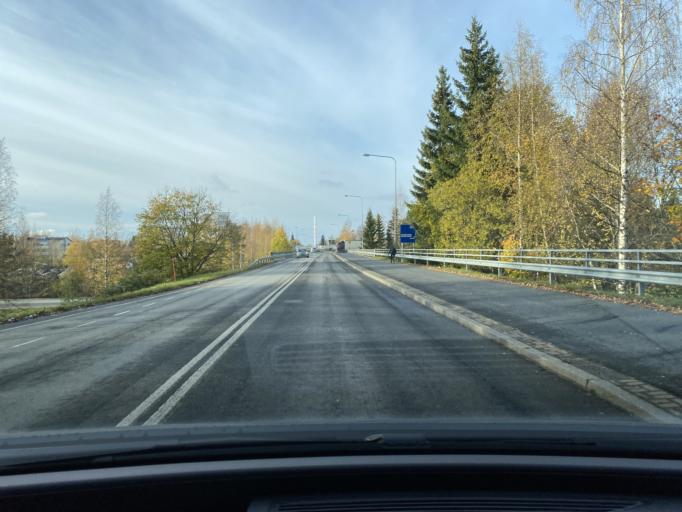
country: FI
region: Pirkanmaa
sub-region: Tampere
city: Lempaeaelae
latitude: 61.3111
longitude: 23.7626
